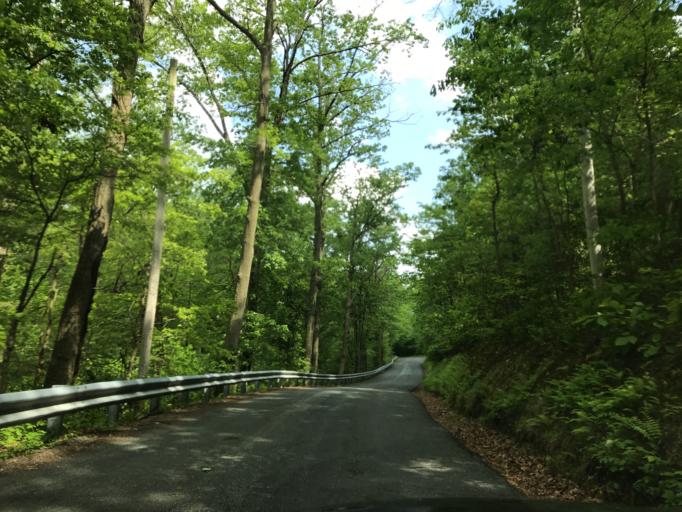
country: US
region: Pennsylvania
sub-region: York County
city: Susquehanna Trails
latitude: 39.6874
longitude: -76.3699
